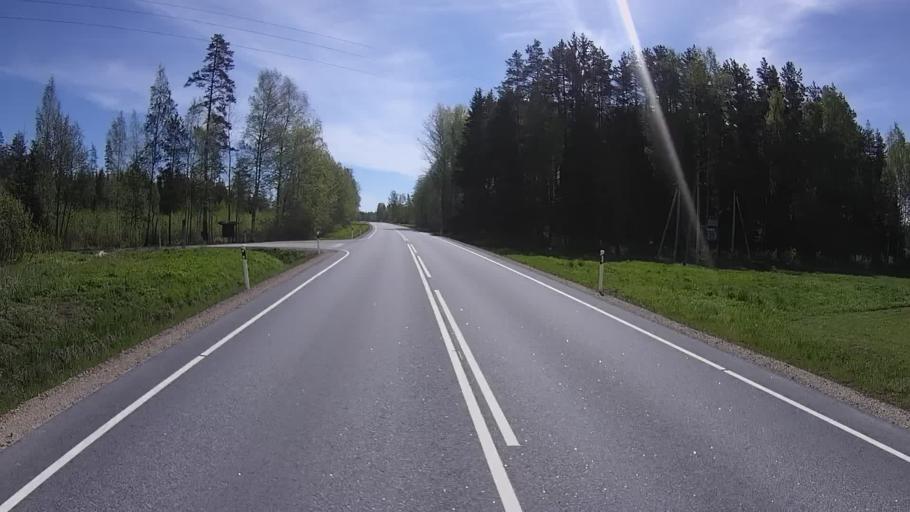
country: EE
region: Polvamaa
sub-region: Raepina vald
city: Rapina
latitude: 57.9806
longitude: 27.2773
